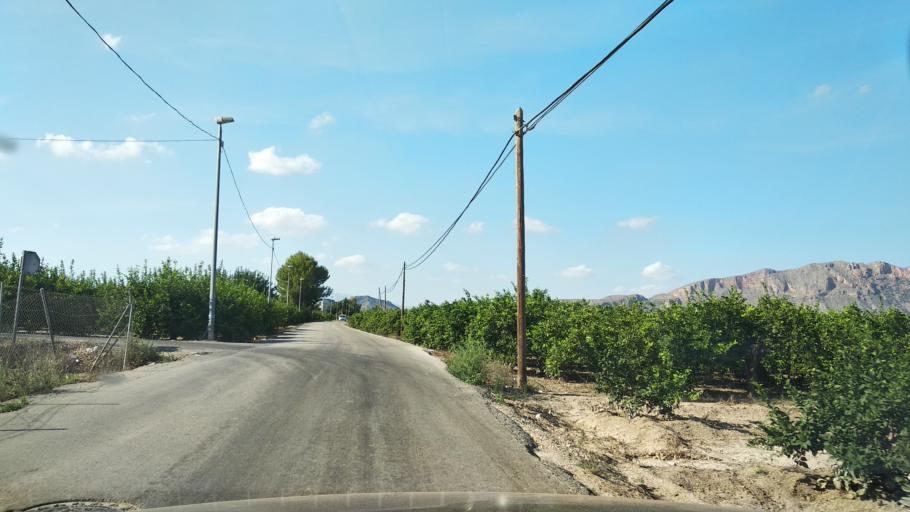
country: ES
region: Murcia
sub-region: Murcia
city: Santomera
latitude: 38.0484
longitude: -1.0391
